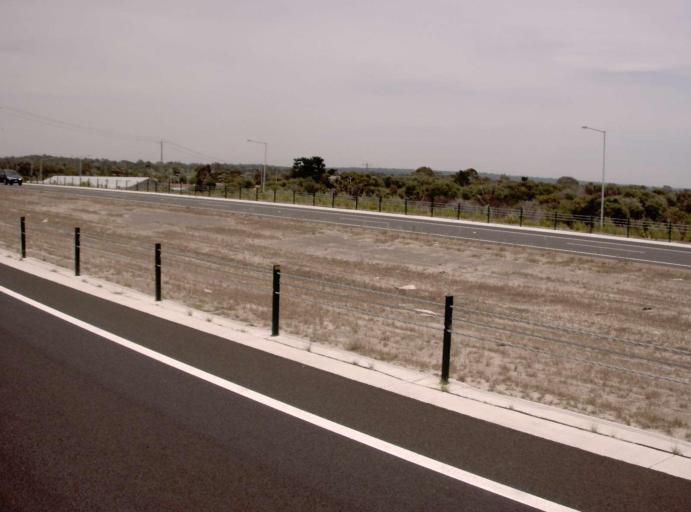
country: AU
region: Victoria
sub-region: Frankston
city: Carrum Downs
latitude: -38.1075
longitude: 145.1611
